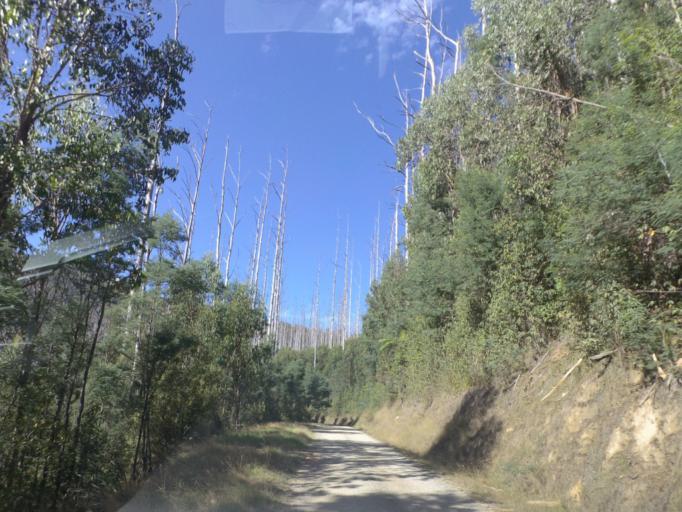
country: AU
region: Victoria
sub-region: Yarra Ranges
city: Millgrove
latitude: -37.5001
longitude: 145.8060
